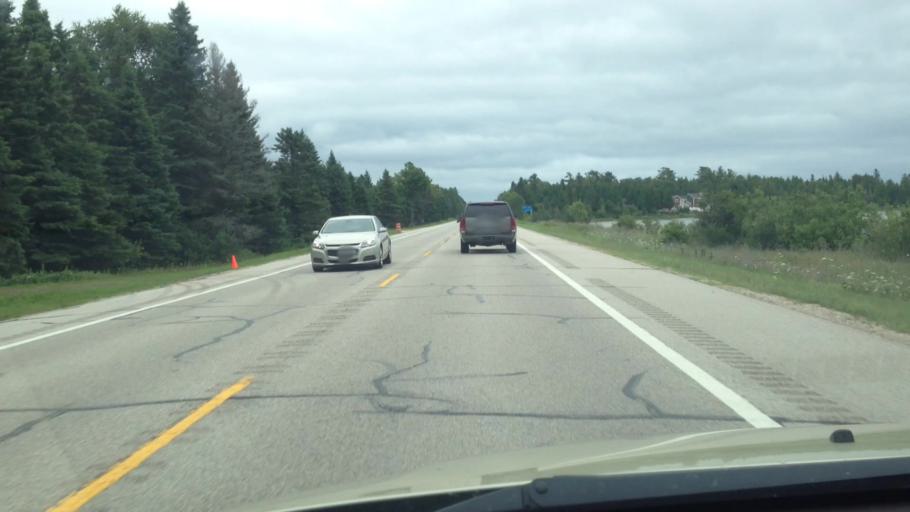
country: US
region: Michigan
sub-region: Luce County
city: Newberry
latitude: 46.1024
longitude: -85.4144
